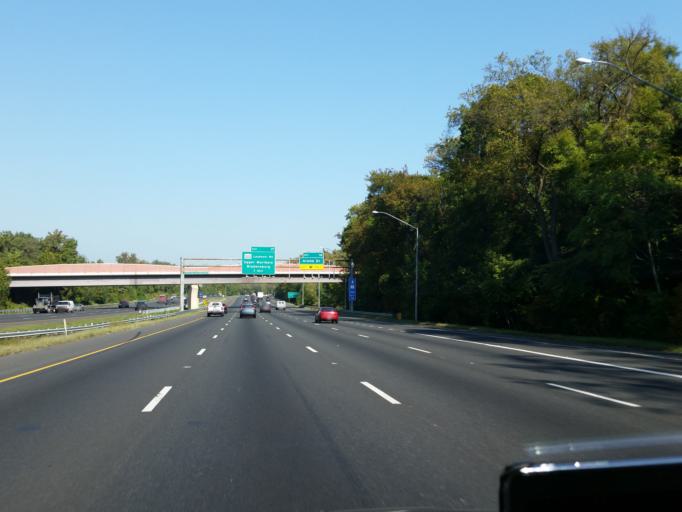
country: US
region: Maryland
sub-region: Prince George's County
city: Largo
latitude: 38.8954
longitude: -76.8482
